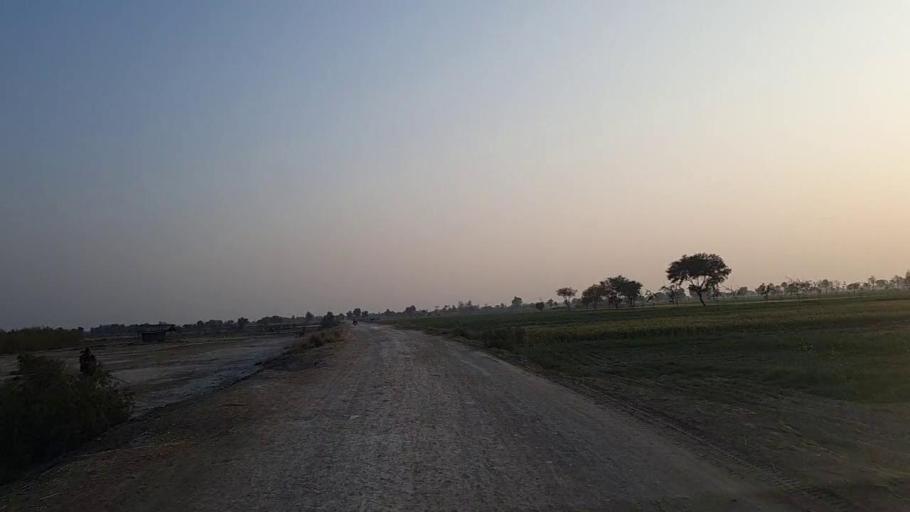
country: PK
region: Sindh
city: Daur
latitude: 26.4247
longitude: 68.3679
